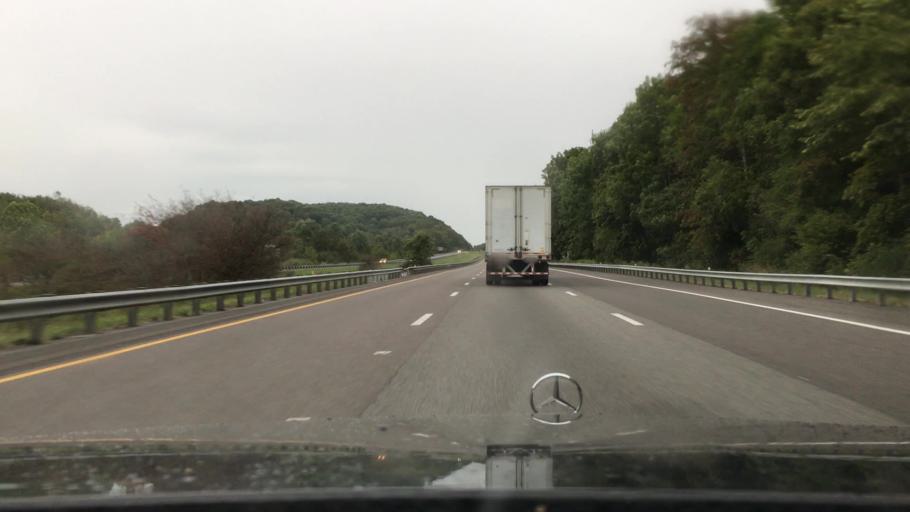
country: US
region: Virginia
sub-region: Smyth County
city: Atkins
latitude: 36.8868
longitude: -81.3764
